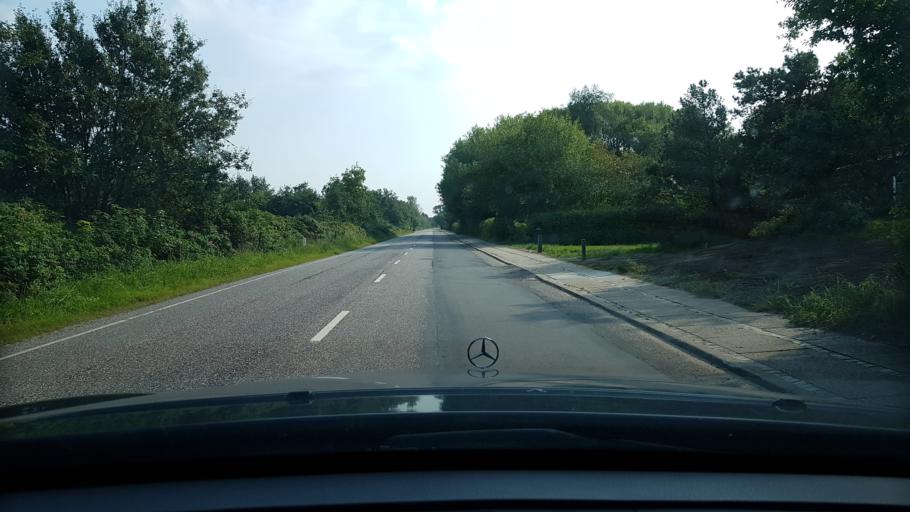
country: DK
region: North Denmark
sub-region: Mariagerfjord Kommune
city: Hadsund
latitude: 56.8153
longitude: 10.2709
